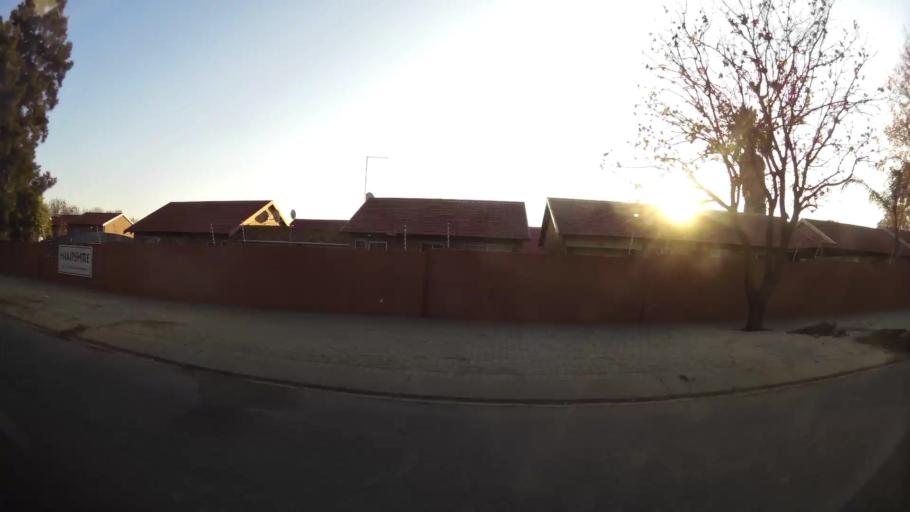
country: ZA
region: Orange Free State
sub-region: Mangaung Metropolitan Municipality
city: Bloemfontein
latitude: -29.0878
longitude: 26.1559
